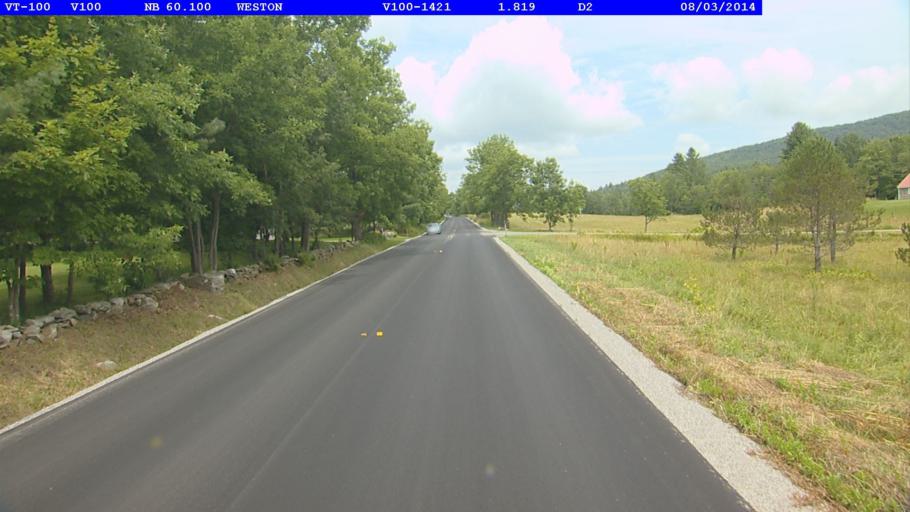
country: US
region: Vermont
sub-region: Windsor County
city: Chester
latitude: 43.2726
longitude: -72.7887
